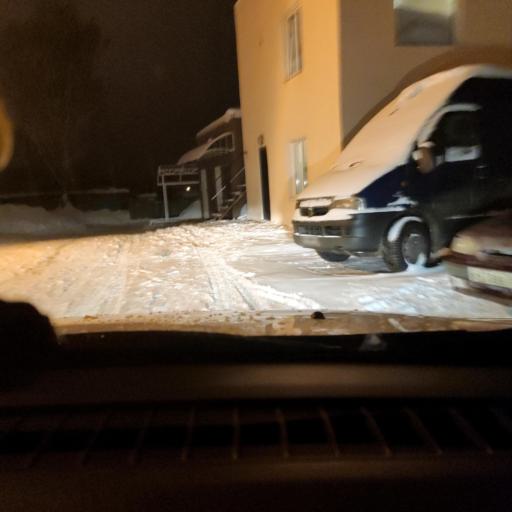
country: RU
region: Samara
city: Novosemeykino
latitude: 53.3307
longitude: 50.3197
